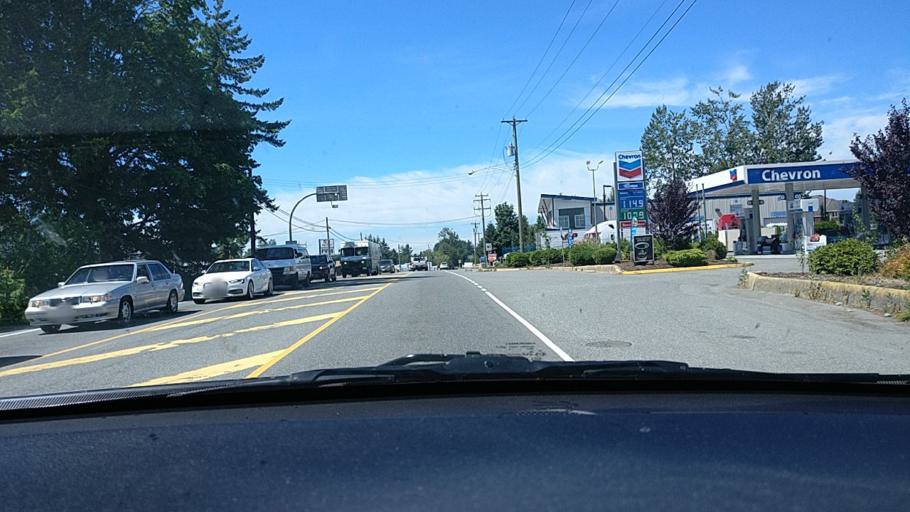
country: CA
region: British Columbia
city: Aldergrove
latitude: 49.0570
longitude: -122.4269
